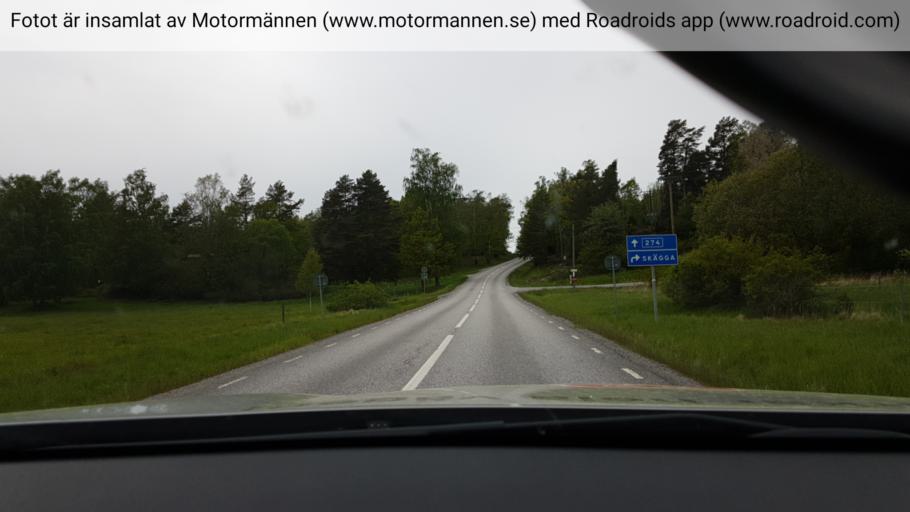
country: SE
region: Stockholm
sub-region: Varmdo Kommun
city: Mortnas
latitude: 59.3937
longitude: 18.4678
